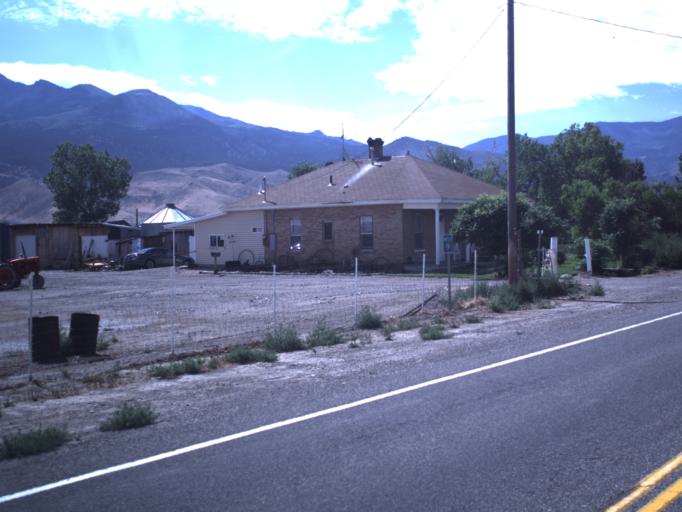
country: US
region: Utah
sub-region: Sevier County
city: Monroe
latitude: 38.6735
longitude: -112.1210
